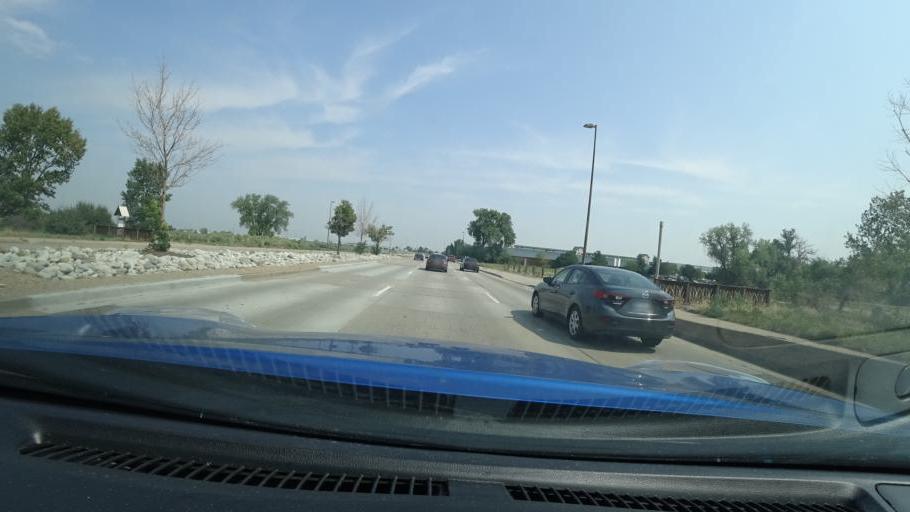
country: US
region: Colorado
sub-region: Adams County
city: Aurora
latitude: 39.7481
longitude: -104.7912
